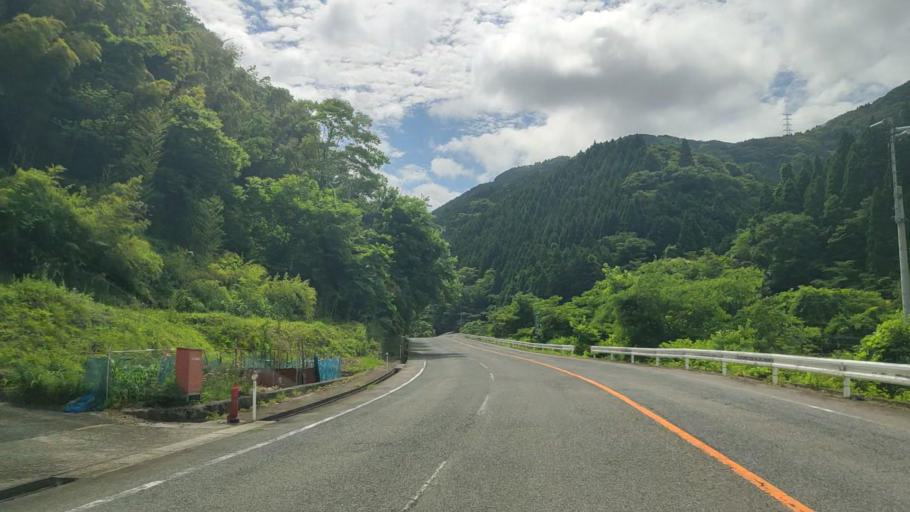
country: JP
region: Okayama
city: Niimi
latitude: 35.2046
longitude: 133.4969
